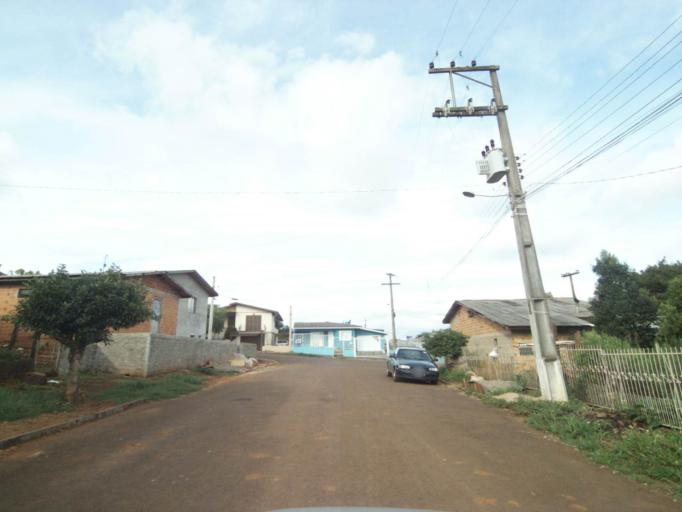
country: BR
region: Rio Grande do Sul
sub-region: Lagoa Vermelha
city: Lagoa Vermelha
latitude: -28.2061
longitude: -51.5324
